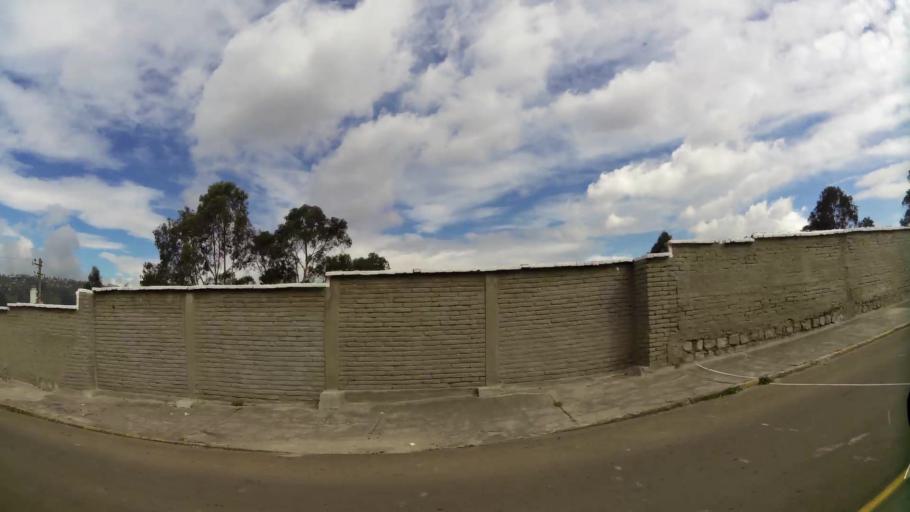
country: EC
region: Pichincha
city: Quito
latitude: -0.2183
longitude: -78.4932
